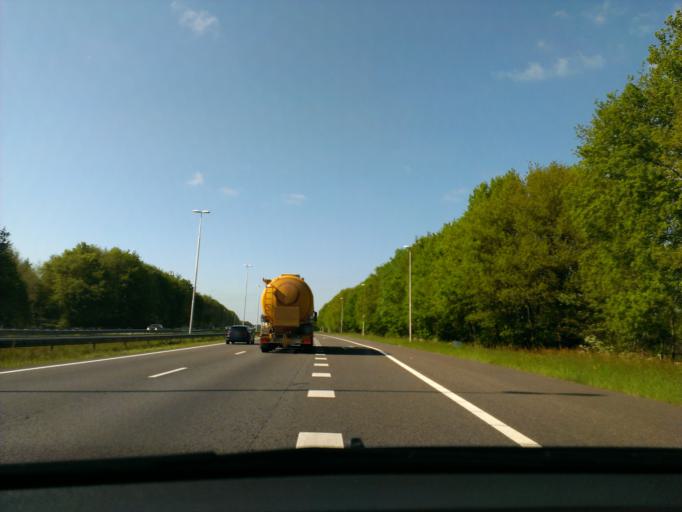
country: NL
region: Gelderland
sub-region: Gemeente Heerde
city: Heerde
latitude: 52.3674
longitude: 6.0258
